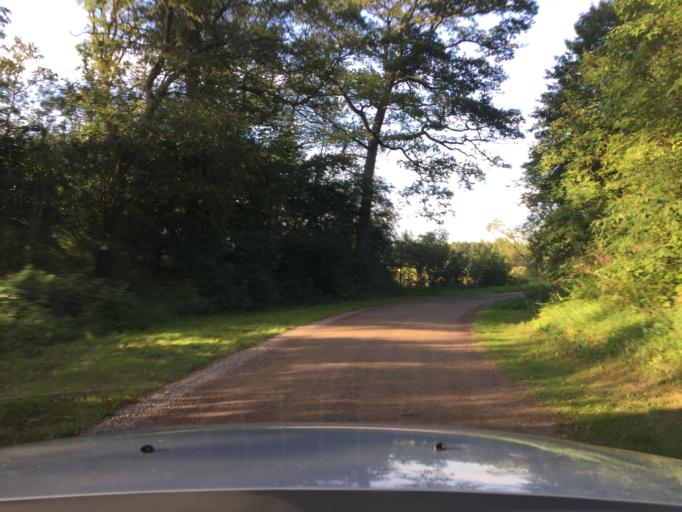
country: SE
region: Skane
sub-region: Hassleholms Kommun
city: Sosdala
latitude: 56.0250
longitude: 13.6915
